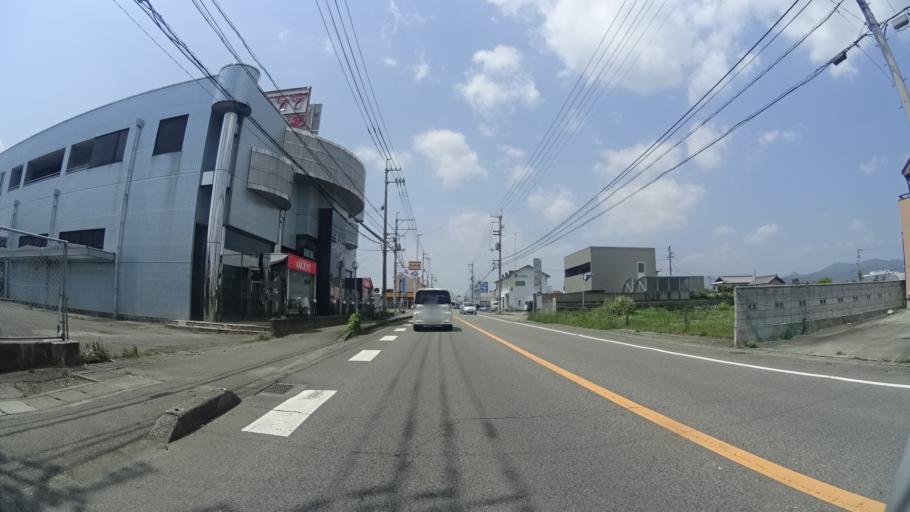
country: JP
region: Tokushima
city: Kamojimacho-jogejima
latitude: 34.0686
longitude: 134.3446
